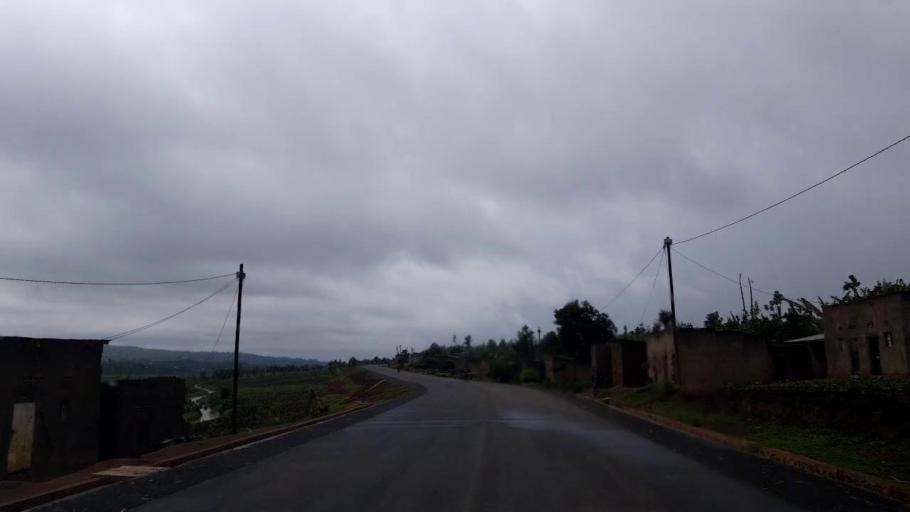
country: RW
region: Northern Province
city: Byumba
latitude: -1.4268
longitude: 30.2766
